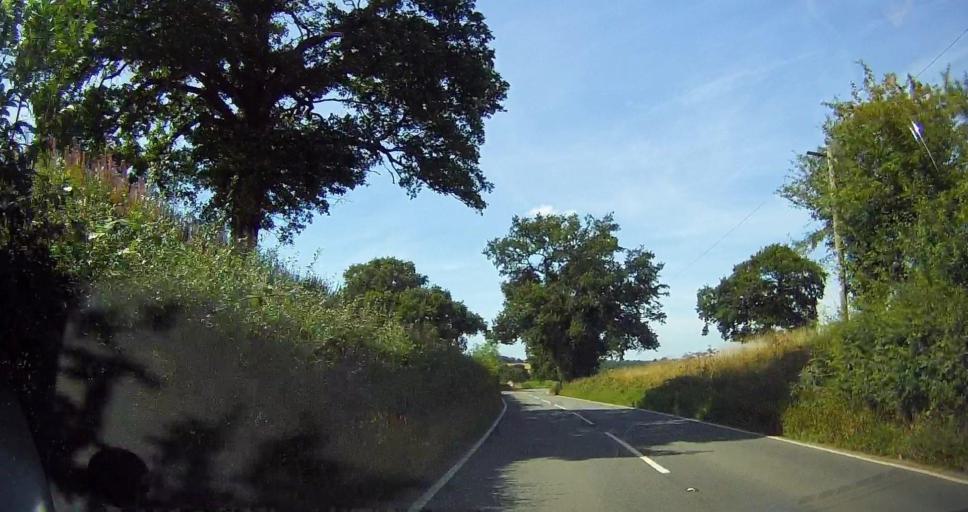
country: GB
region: England
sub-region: Shropshire
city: Market Drayton
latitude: 52.9605
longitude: -2.5131
